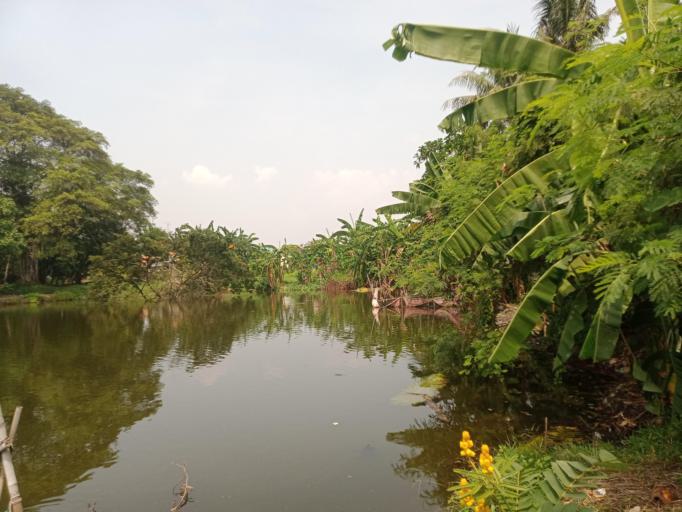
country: ID
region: West Java
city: Sepatan
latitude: -6.1063
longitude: 106.5708
